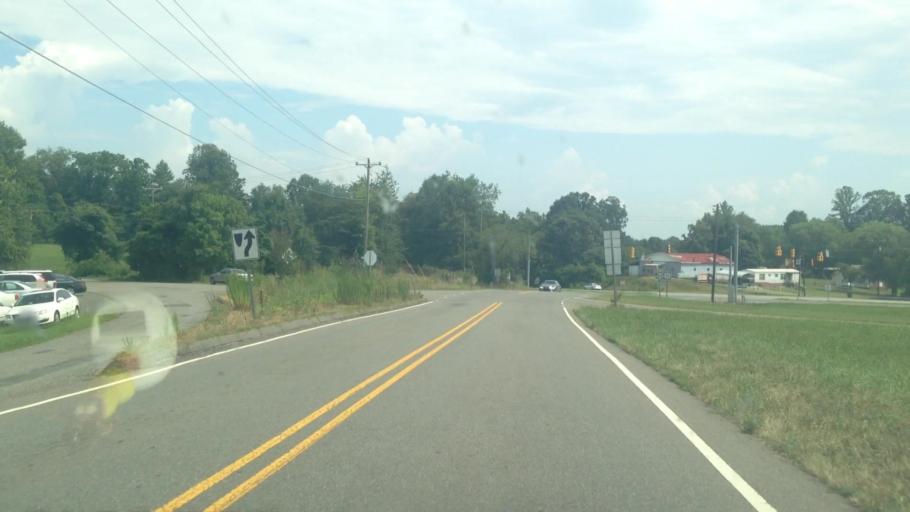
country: US
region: North Carolina
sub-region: Surry County
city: Flat Rock
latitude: 36.4716
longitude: -80.5735
